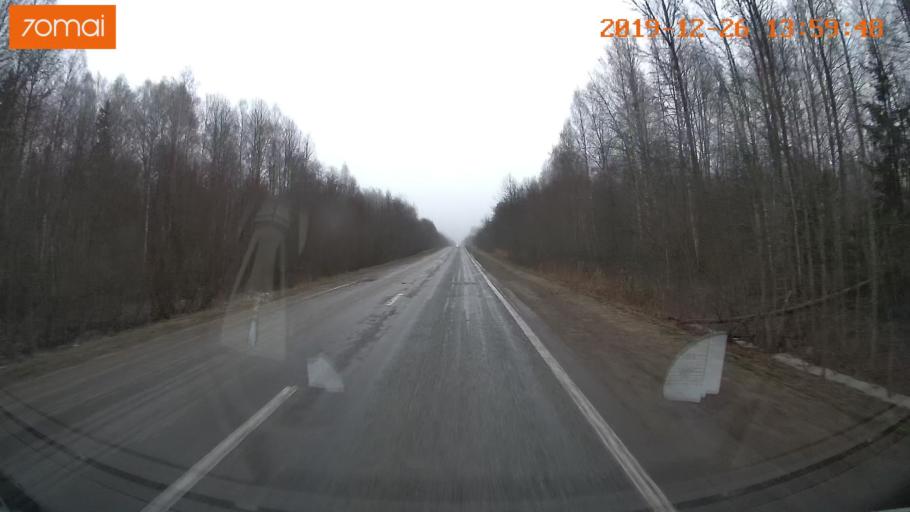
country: RU
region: Jaroslavl
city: Poshekhon'ye
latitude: 58.5628
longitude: 38.7310
